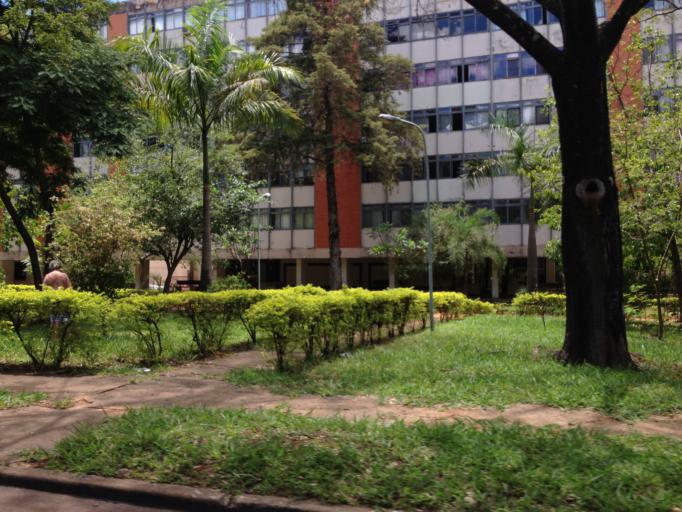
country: BR
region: Federal District
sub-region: Brasilia
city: Brasilia
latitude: -15.8256
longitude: -47.9184
